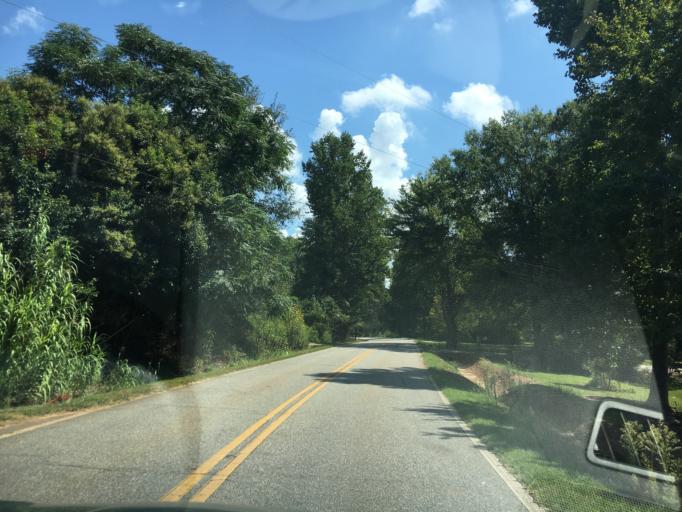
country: US
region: South Carolina
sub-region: Spartanburg County
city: Wellford
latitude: 34.8936
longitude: -82.0648
